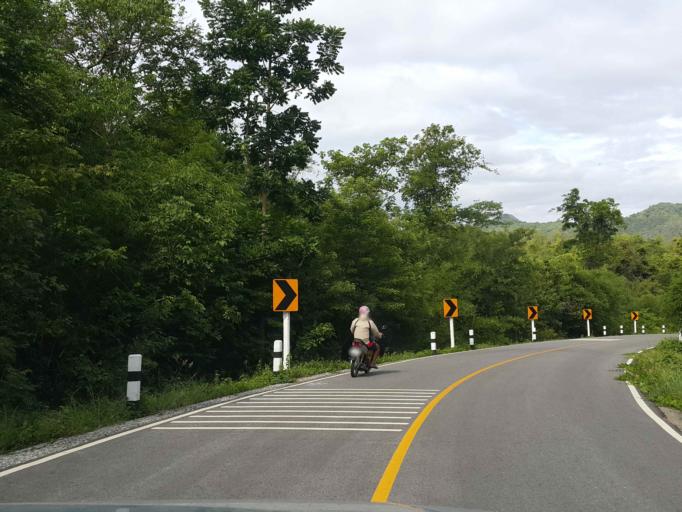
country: TH
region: Sukhothai
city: Thung Saliam
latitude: 17.2456
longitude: 99.4912
